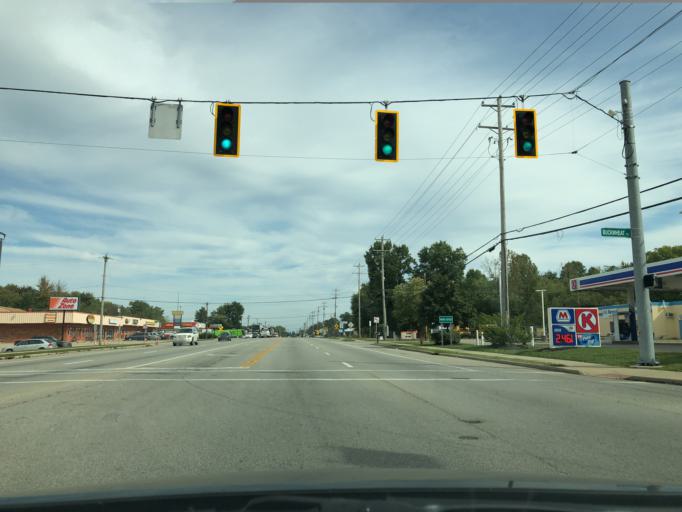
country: US
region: Ohio
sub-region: Clermont County
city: Mount Repose
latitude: 39.1995
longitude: -84.2265
